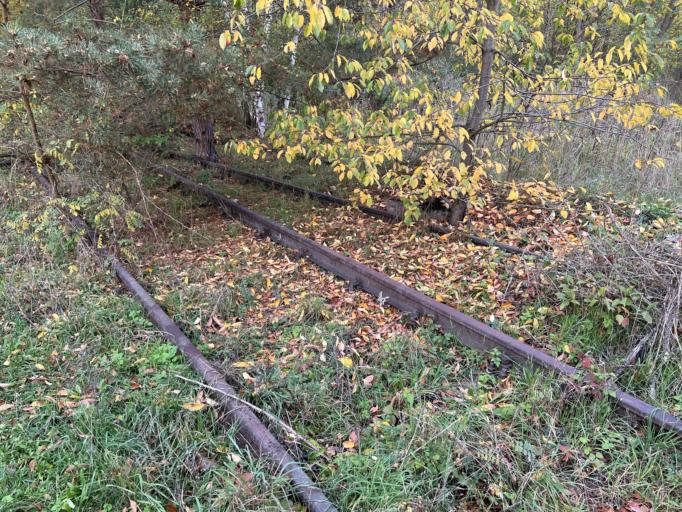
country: DE
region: Brandenburg
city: Konigs Wusterhausen
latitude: 52.2804
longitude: 13.6188
